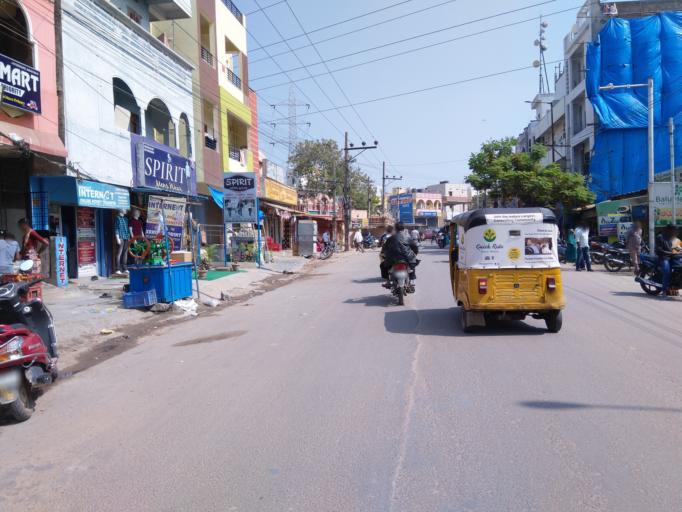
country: IN
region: Telangana
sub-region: Rangareddi
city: Kukatpalli
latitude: 17.5024
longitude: 78.4196
